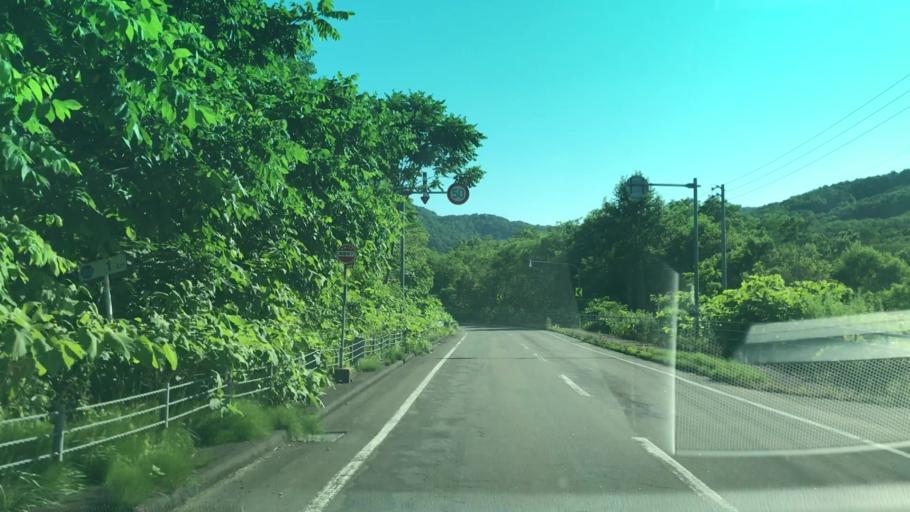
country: JP
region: Hokkaido
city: Yoichi
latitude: 43.0687
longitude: 140.7064
